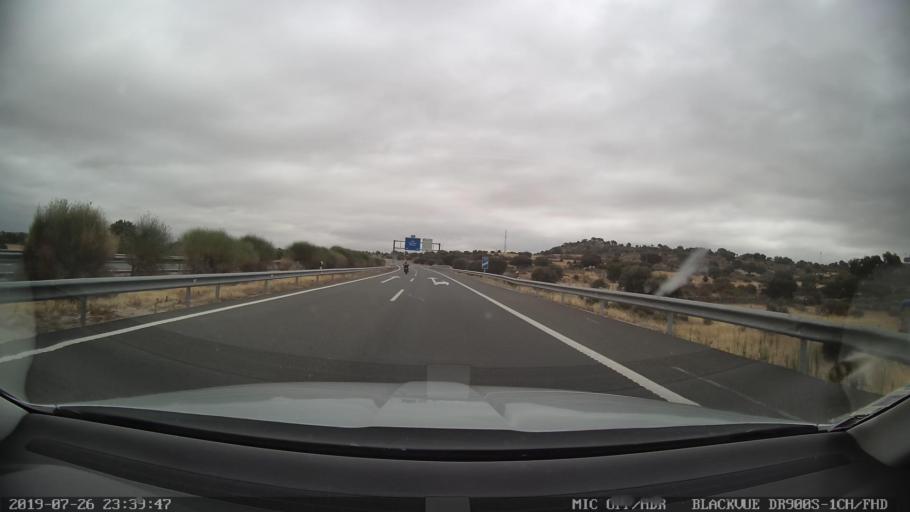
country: ES
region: Extremadura
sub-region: Provincia de Caceres
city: Trujillo
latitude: 39.4534
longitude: -5.8668
